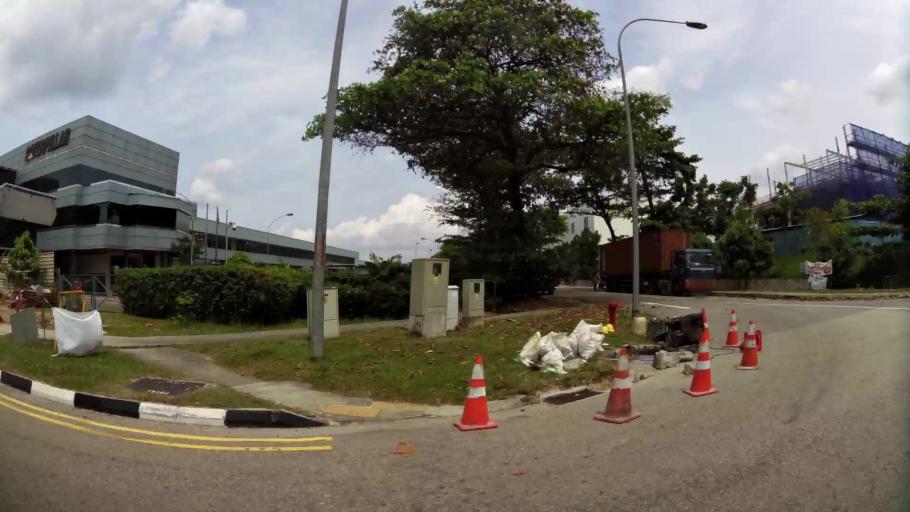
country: SG
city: Singapore
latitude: 1.3222
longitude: 103.7059
